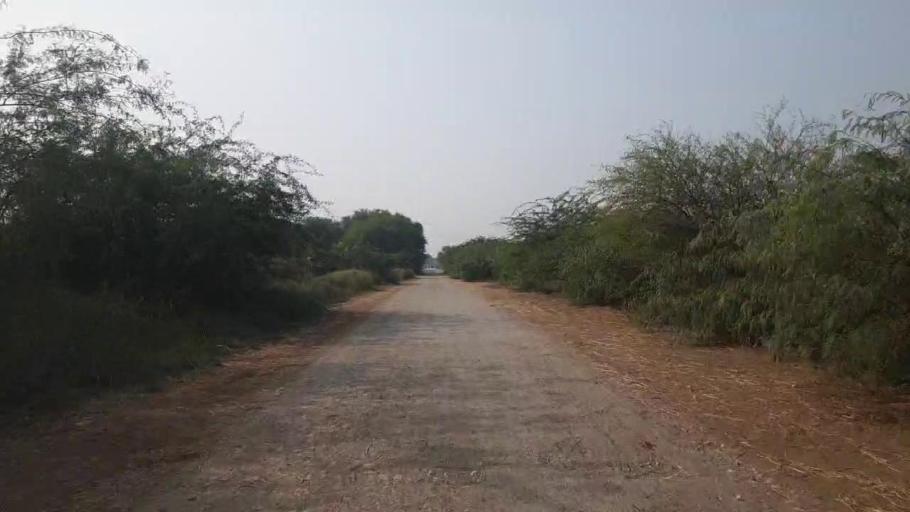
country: PK
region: Sindh
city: Tando Jam
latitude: 25.2809
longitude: 68.4950
